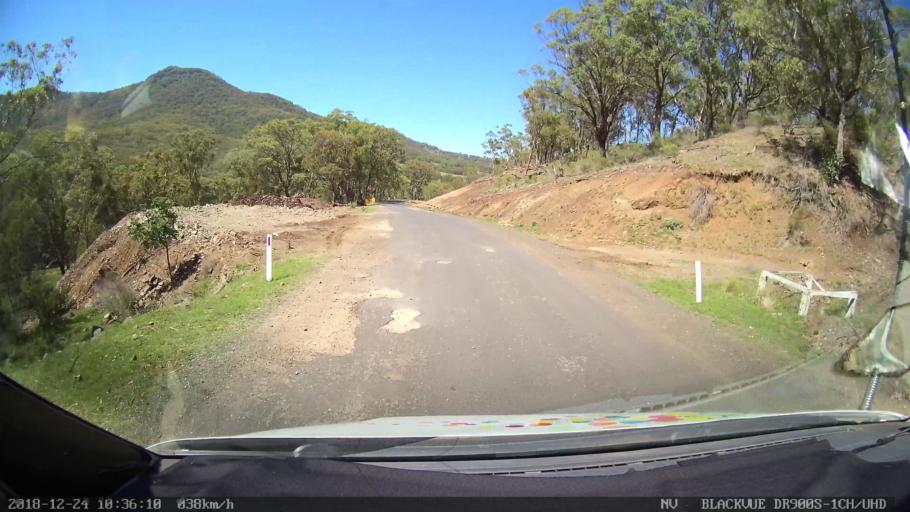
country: AU
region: New South Wales
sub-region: Upper Hunter Shire
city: Merriwa
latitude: -31.8429
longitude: 150.5007
